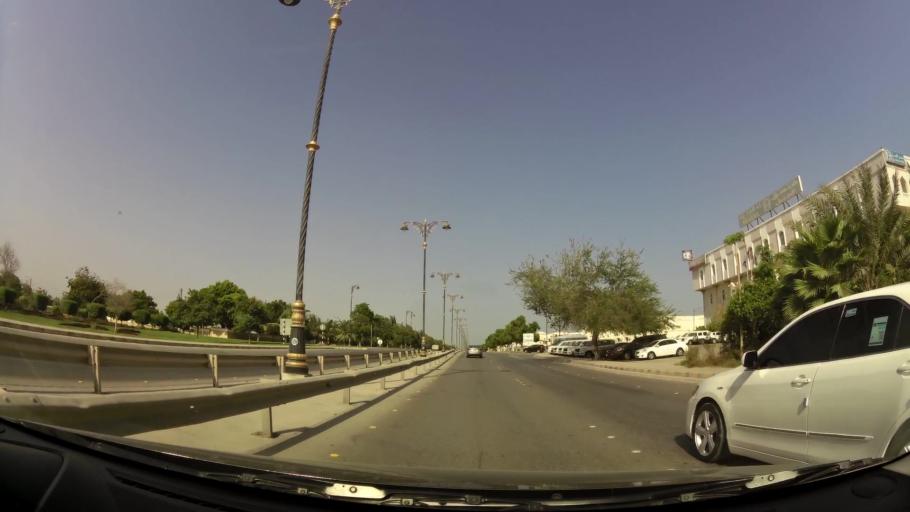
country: OM
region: Zufar
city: Salalah
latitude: 17.0046
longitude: 54.0448
